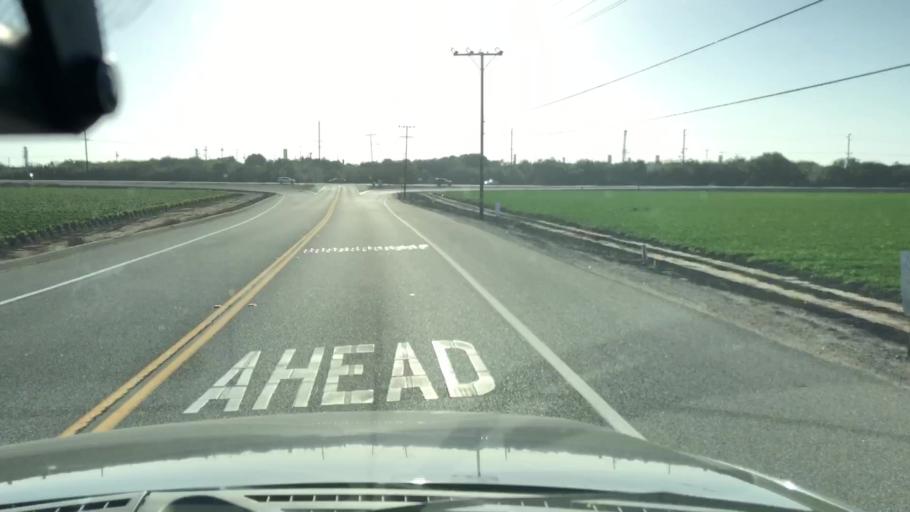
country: US
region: California
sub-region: Ventura County
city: Oxnard Shores
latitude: 34.2192
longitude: -119.2514
